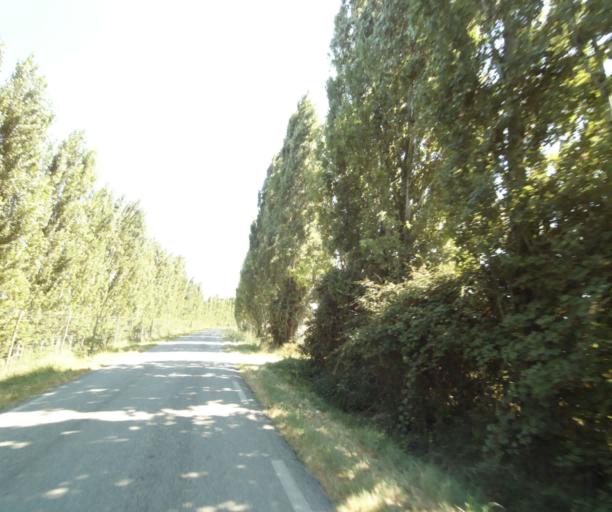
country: FR
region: Languedoc-Roussillon
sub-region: Departement de l'Herault
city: Marsillargues
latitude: 43.6483
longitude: 4.1707
